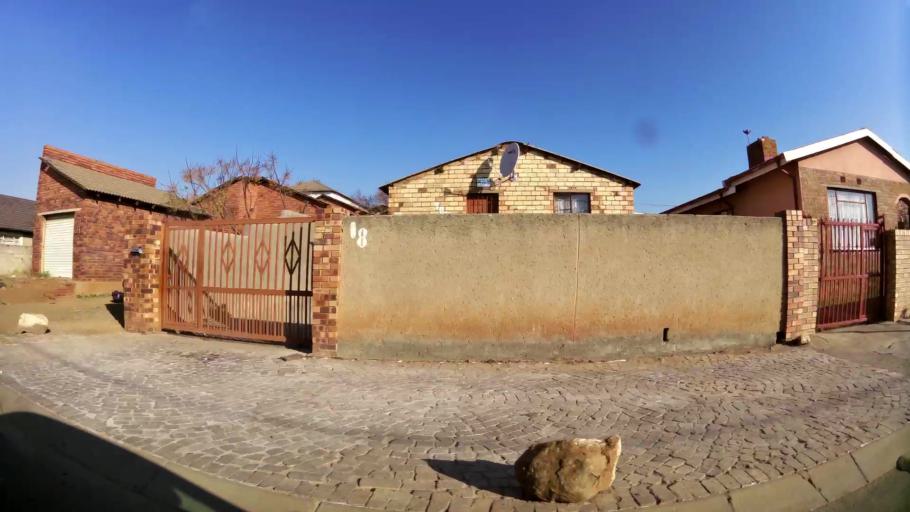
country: ZA
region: Gauteng
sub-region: City of Johannesburg Metropolitan Municipality
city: Soweto
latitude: -26.2675
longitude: 27.8688
